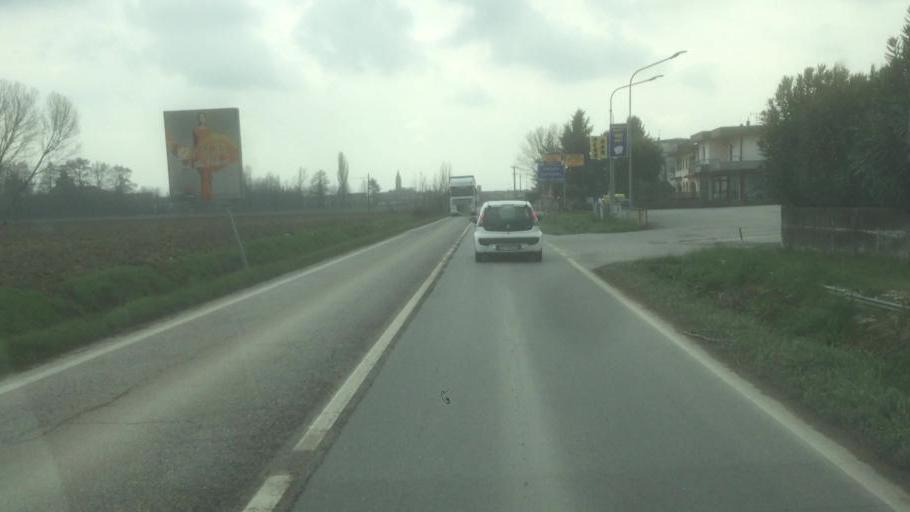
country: IT
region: Lombardy
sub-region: Provincia di Mantova
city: Casaloldo
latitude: 45.2636
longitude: 10.4773
